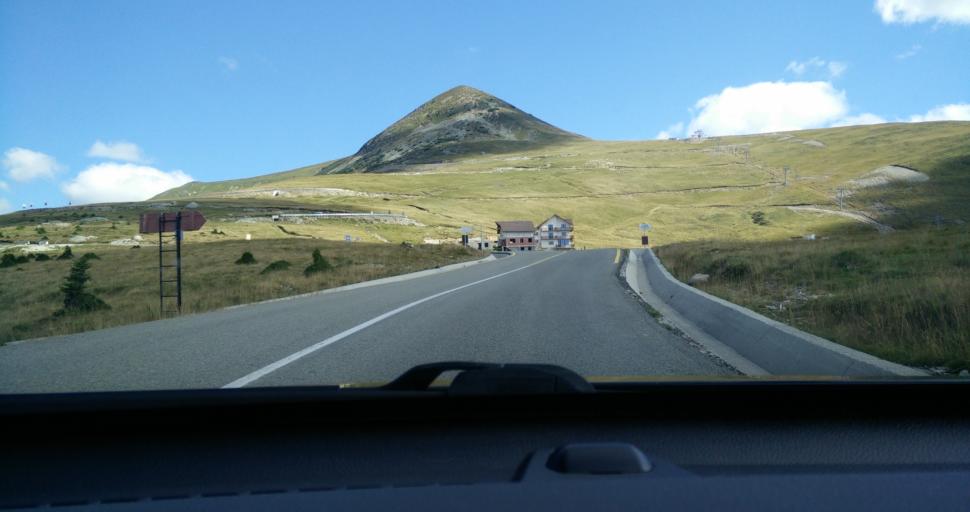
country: RO
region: Gorj
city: Novaci-Straini
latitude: 45.3125
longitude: 23.6826
